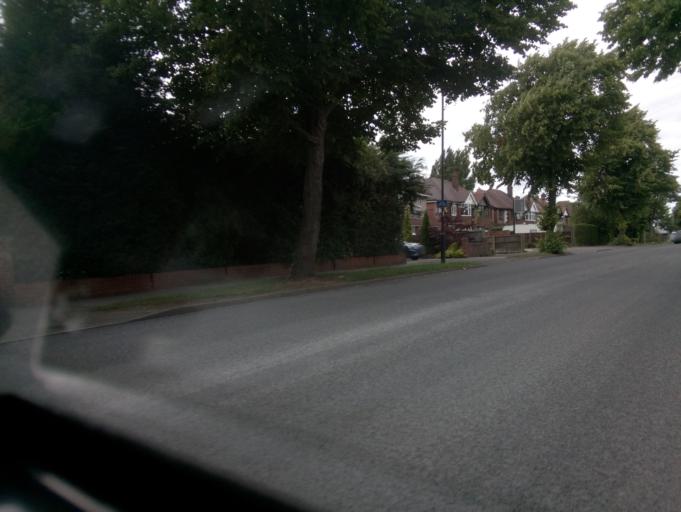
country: GB
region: England
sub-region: Warwickshire
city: Nuneaton
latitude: 52.5350
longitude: -1.4657
